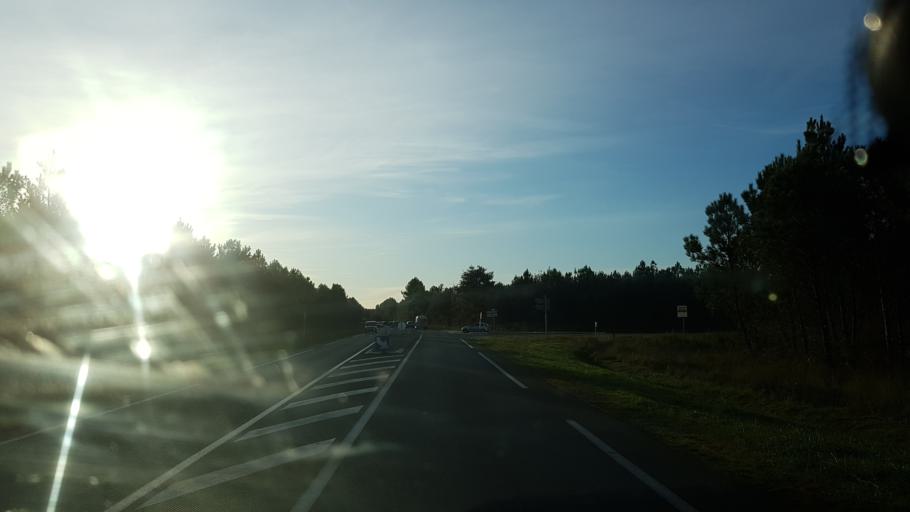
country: FR
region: Aquitaine
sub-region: Departement de la Gironde
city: Martignas-sur-Jalle
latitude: 44.8335
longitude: -0.8222
